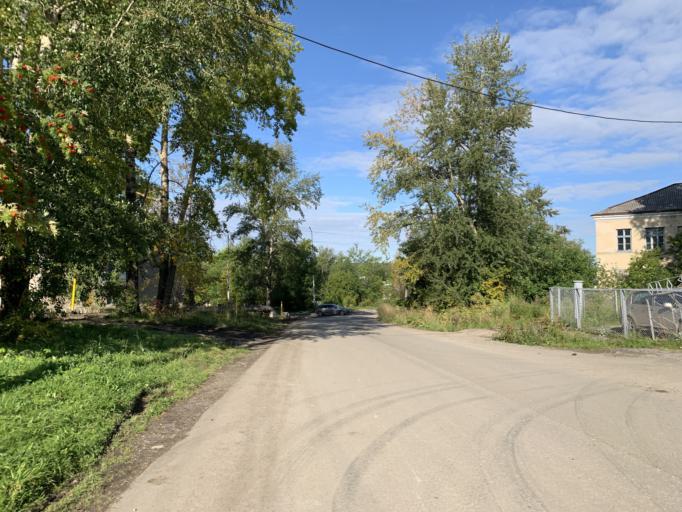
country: RU
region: Perm
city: Gubakha
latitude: 58.8432
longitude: 57.5550
